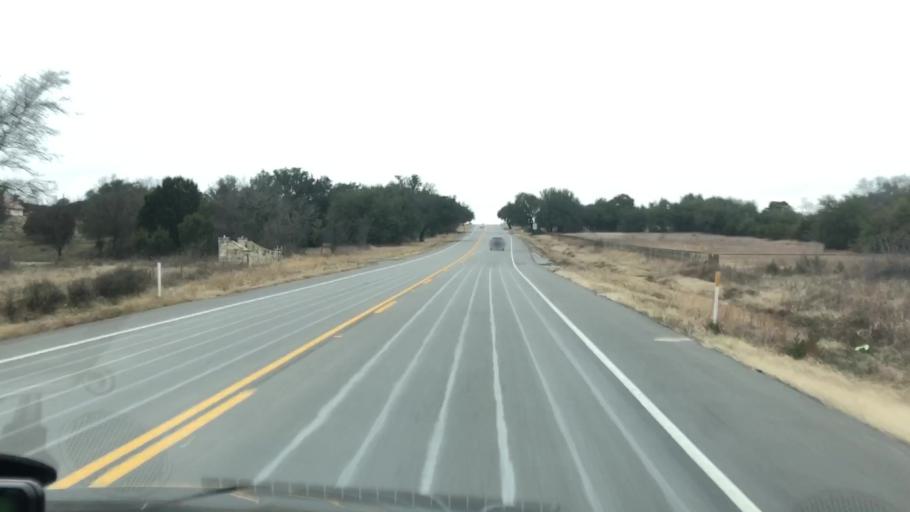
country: US
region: Texas
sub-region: Hamilton County
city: Hico
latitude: 31.9993
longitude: -98.0499
